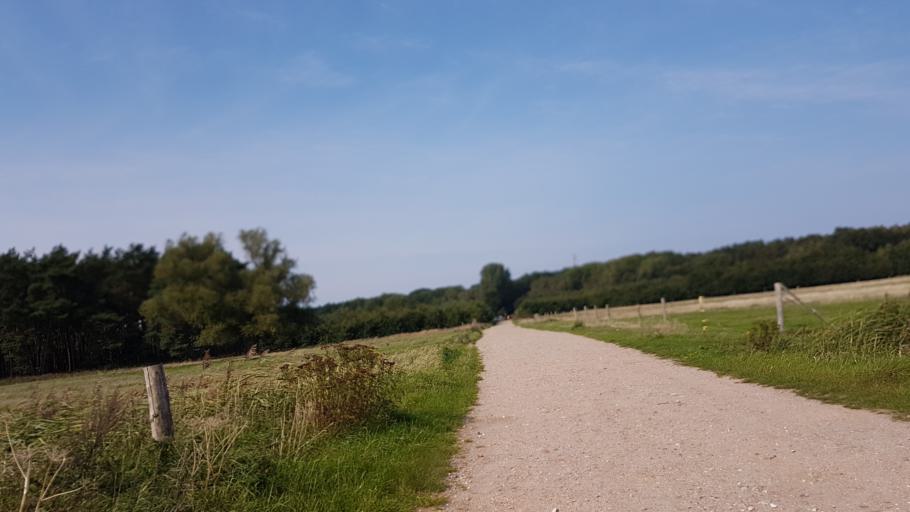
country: DE
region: Mecklenburg-Vorpommern
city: Glowe
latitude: 54.5579
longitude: 13.4630
